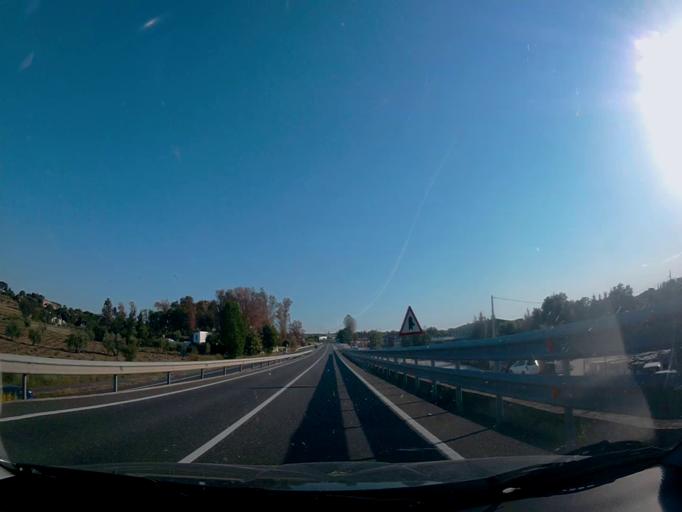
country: ES
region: Castille-La Mancha
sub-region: Province of Toledo
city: Escalona
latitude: 40.1580
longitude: -4.4000
